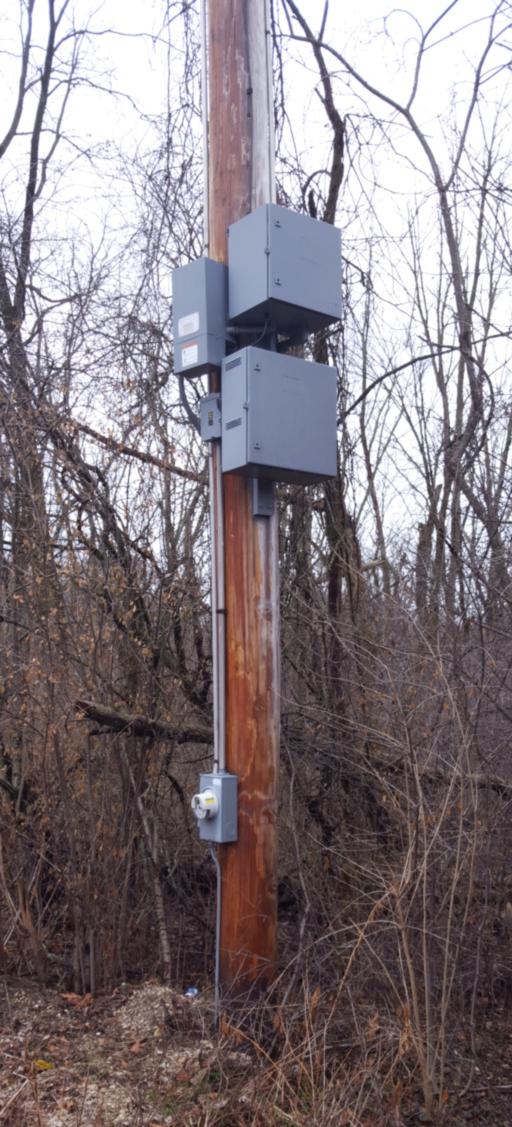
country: US
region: Illinois
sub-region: Cook County
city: Northbrook
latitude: 42.1395
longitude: -87.8094
